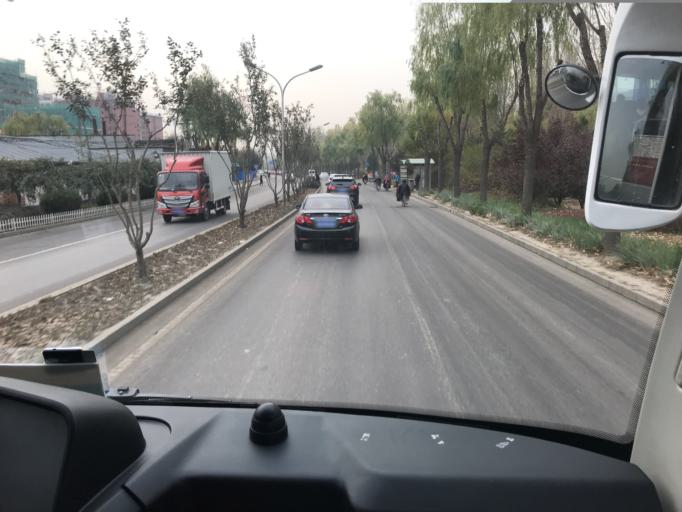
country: CN
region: Beijing
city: Sujiatuo
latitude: 40.0953
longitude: 116.2083
